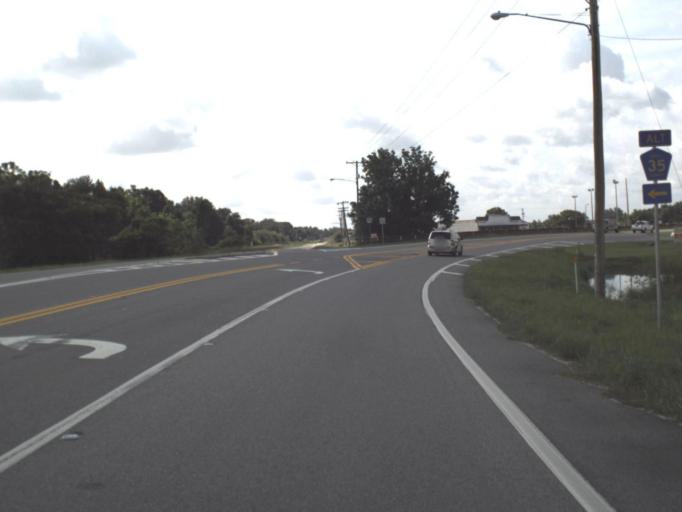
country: US
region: Florida
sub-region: Pasco County
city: Dade City
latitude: 28.3613
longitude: -82.1828
